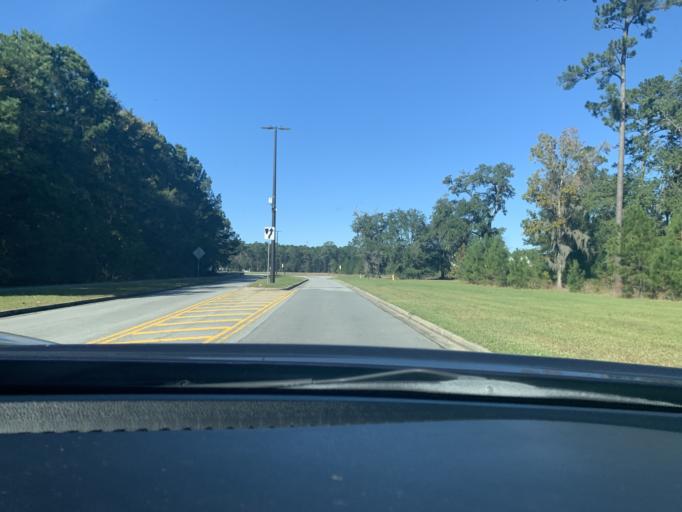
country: US
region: Georgia
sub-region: Chatham County
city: Pooler
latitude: 32.0862
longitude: -81.2741
